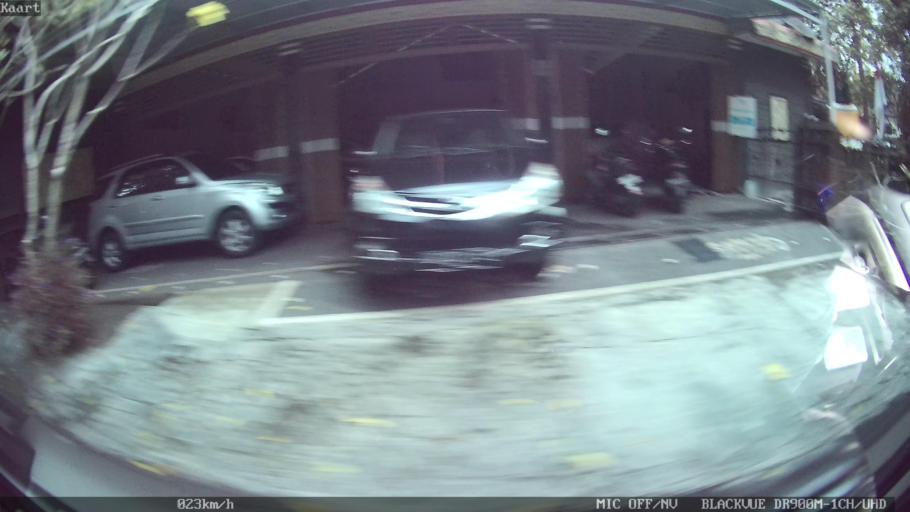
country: ID
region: Bali
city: Banjar Parekan
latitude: -8.5841
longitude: 115.2140
